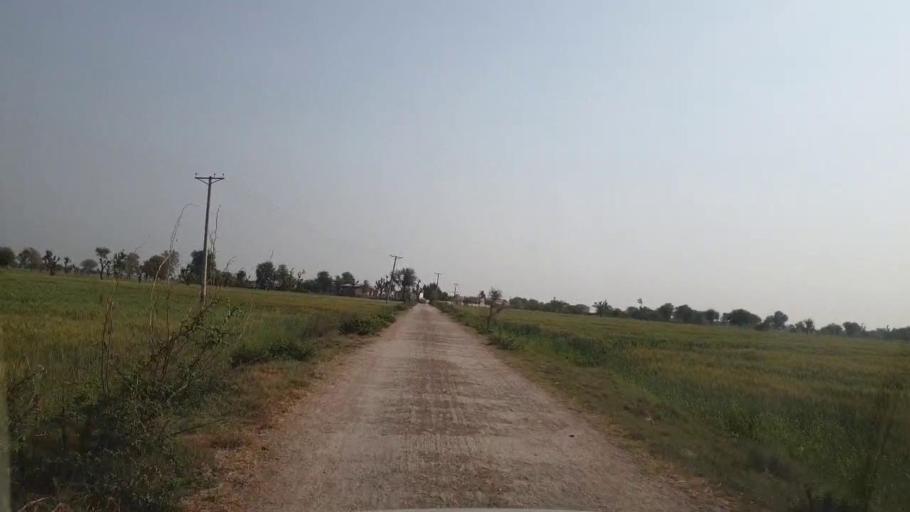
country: PK
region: Sindh
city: Dhoro Naro
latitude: 25.4747
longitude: 69.6464
